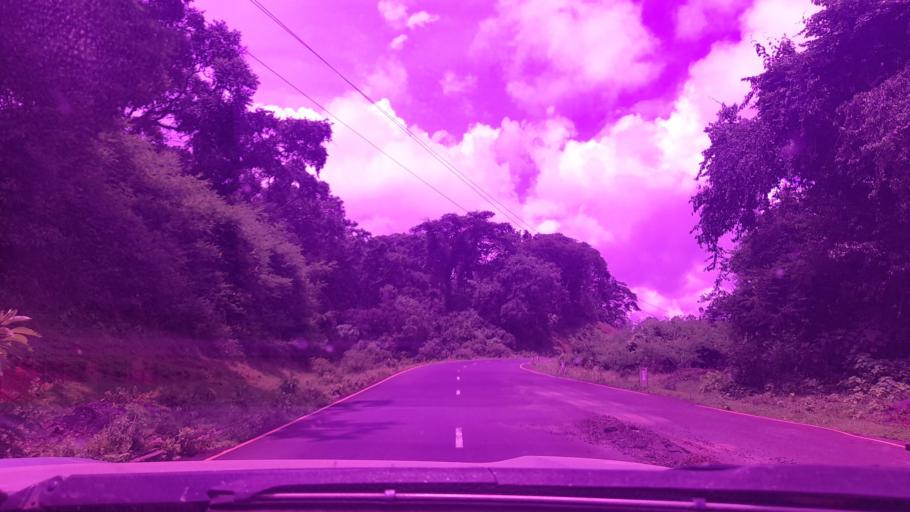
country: ET
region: Oromiya
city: Metu
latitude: 8.3392
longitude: 35.7405
